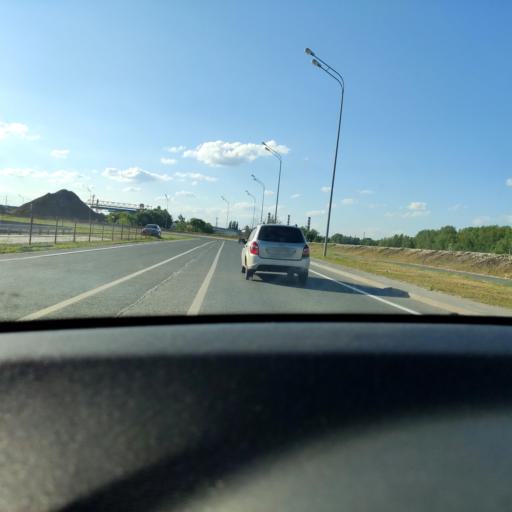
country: RU
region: Samara
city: Smyshlyayevka
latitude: 53.1837
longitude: 50.3057
